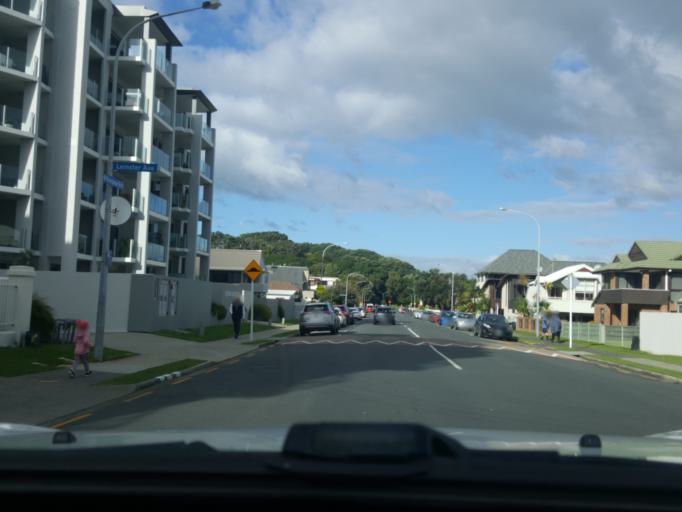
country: NZ
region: Bay of Plenty
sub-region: Tauranga City
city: Tauranga
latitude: -37.6333
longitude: 176.1786
